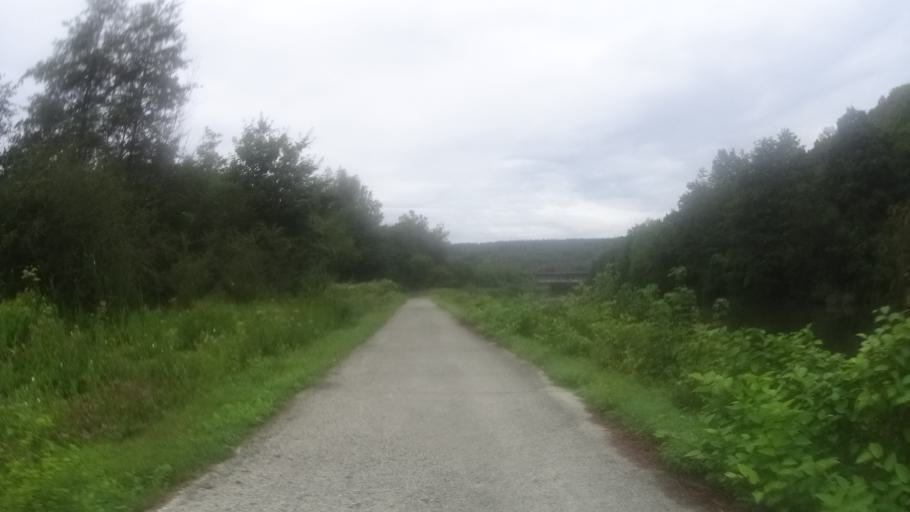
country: BE
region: Wallonia
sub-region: Province du Hainaut
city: Thuin
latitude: 50.3636
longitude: 4.3114
